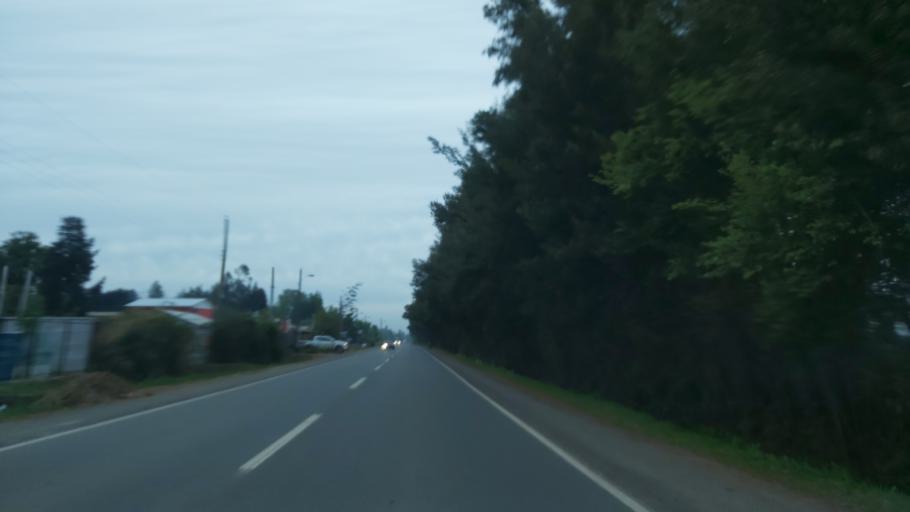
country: CL
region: Maule
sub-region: Provincia de Linares
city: Colbun
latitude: -35.7376
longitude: -71.4902
